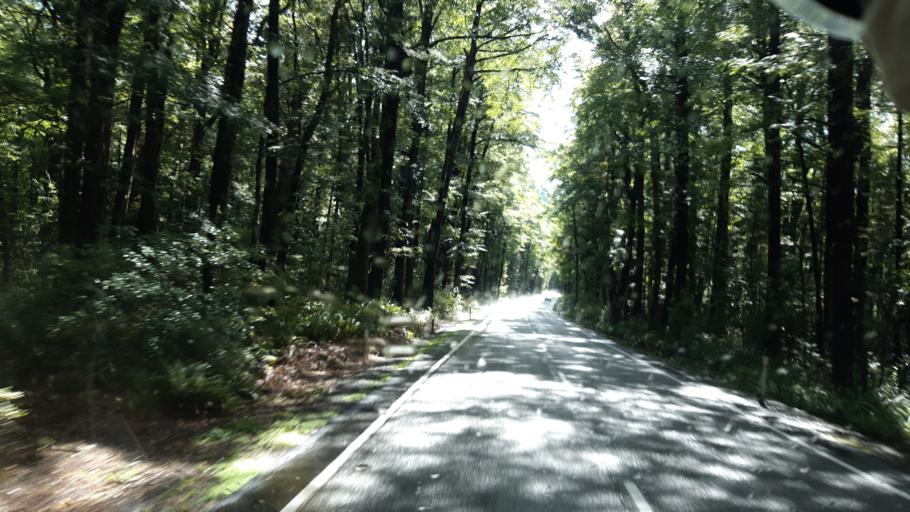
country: NZ
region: Canterbury
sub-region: Hurunui District
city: Amberley
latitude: -42.3771
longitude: 172.2750
